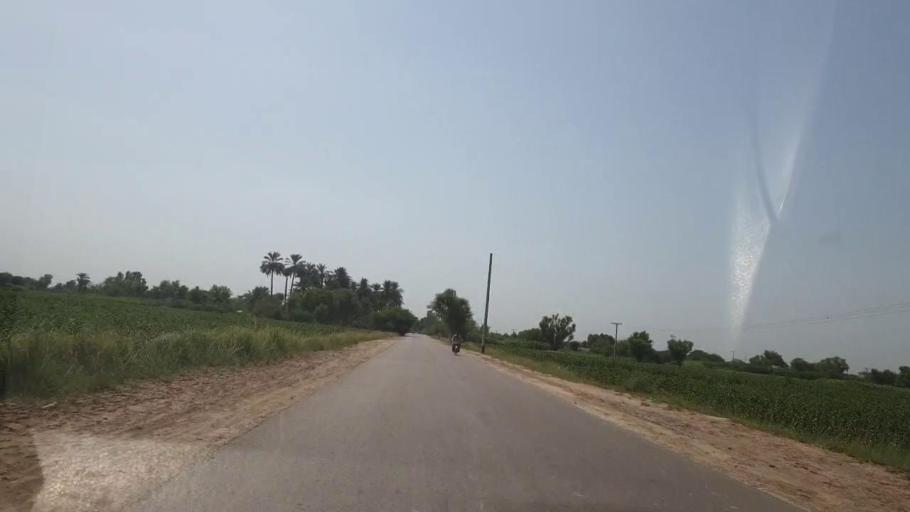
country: PK
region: Sindh
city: Bozdar
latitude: 27.1203
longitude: 68.5499
